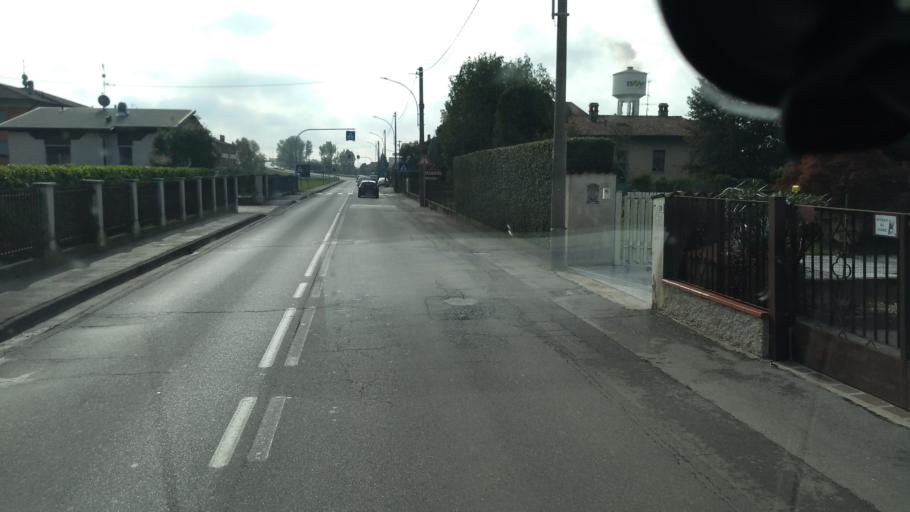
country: IT
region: Lombardy
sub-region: Provincia di Bergamo
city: Vidalengo
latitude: 45.5222
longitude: 9.6395
